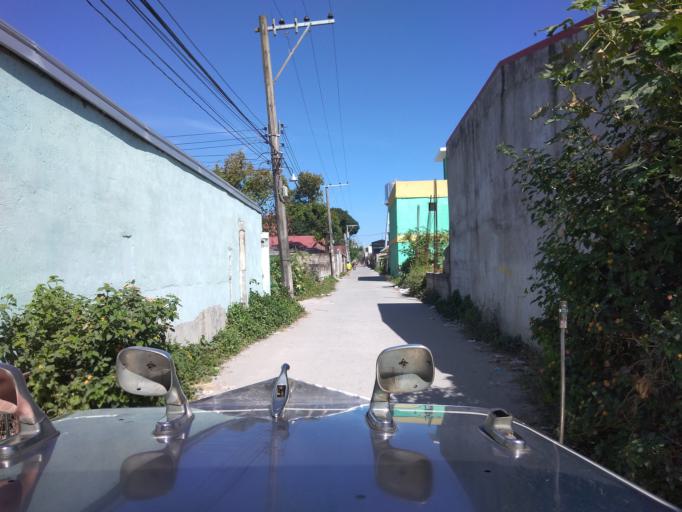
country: PH
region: Central Luzon
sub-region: Province of Pampanga
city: Calibutbut
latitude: 15.1091
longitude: 120.6051
